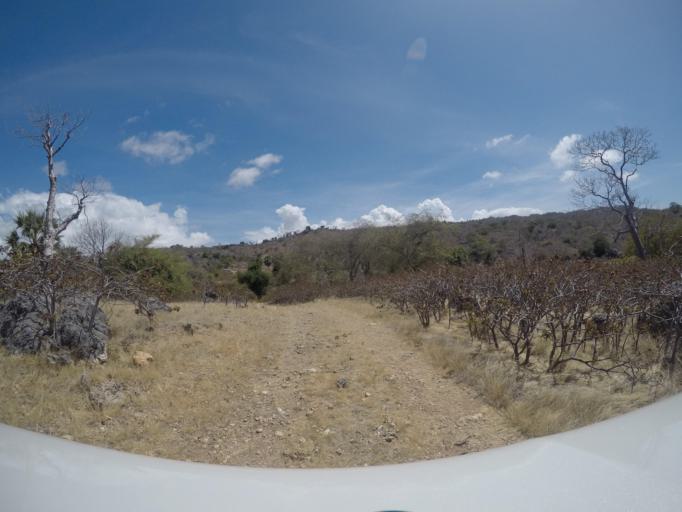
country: TL
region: Baucau
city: Baucau
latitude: -8.4340
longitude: 126.4413
